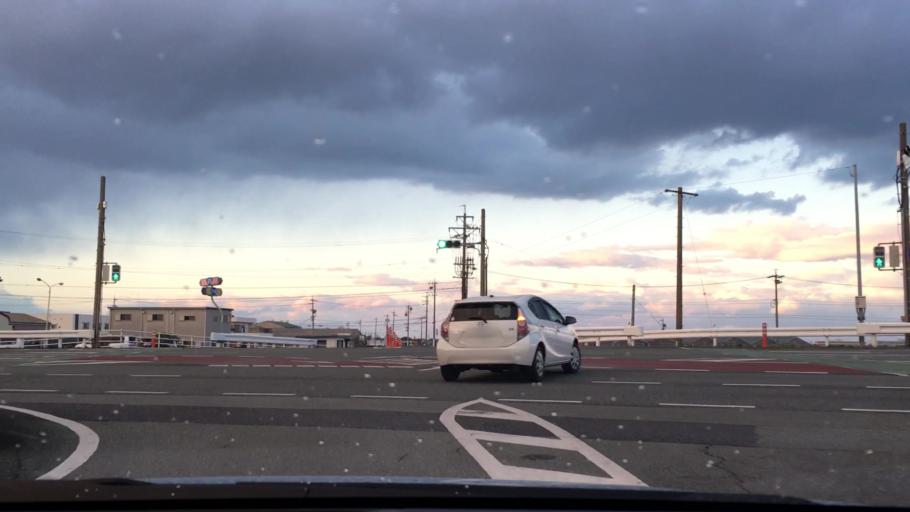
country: JP
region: Mie
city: Ise
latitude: 34.5345
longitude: 136.6787
